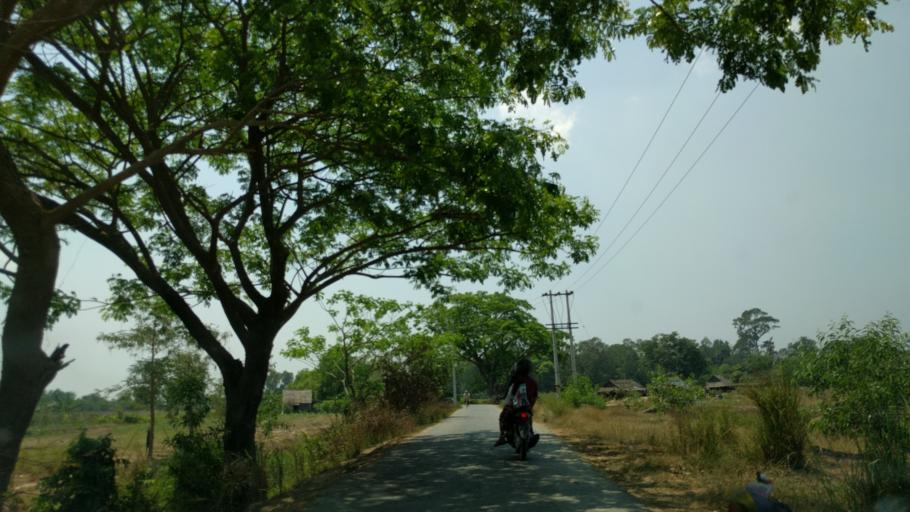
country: MM
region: Mon
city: Martaban
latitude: 16.5887
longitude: 97.6614
